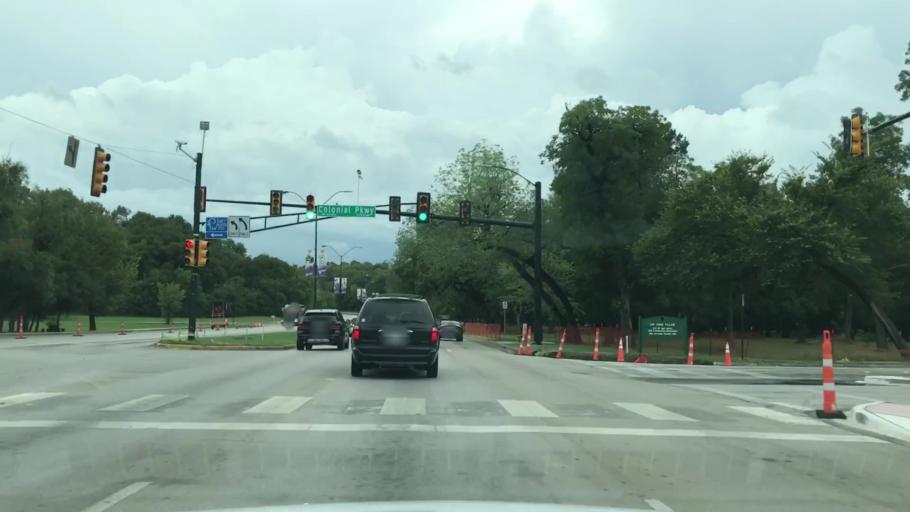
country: US
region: Texas
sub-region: Tarrant County
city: Fort Worth
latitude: 32.7222
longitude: -97.3614
